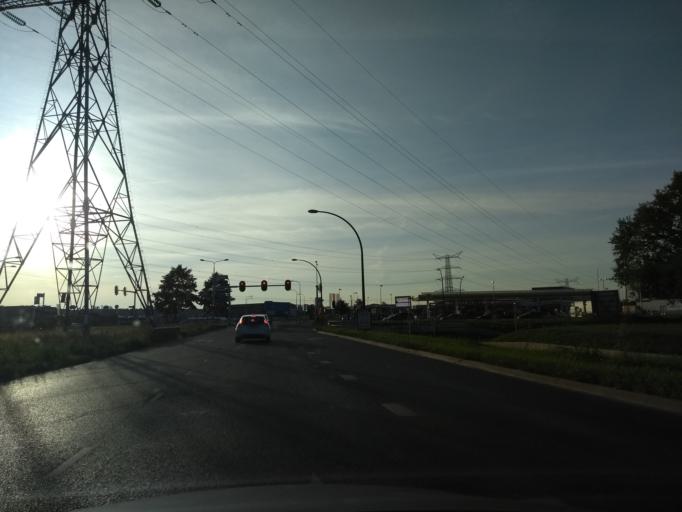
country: NL
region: Overijssel
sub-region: Gemeente Hengelo
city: Hengelo
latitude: 52.2424
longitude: 6.7666
